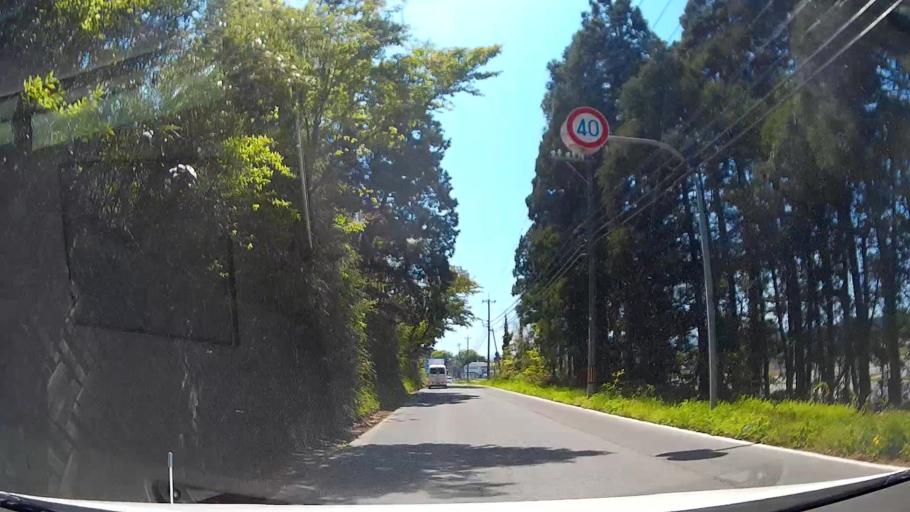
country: JP
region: Ishikawa
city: Nanao
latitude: 37.4523
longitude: 137.2992
